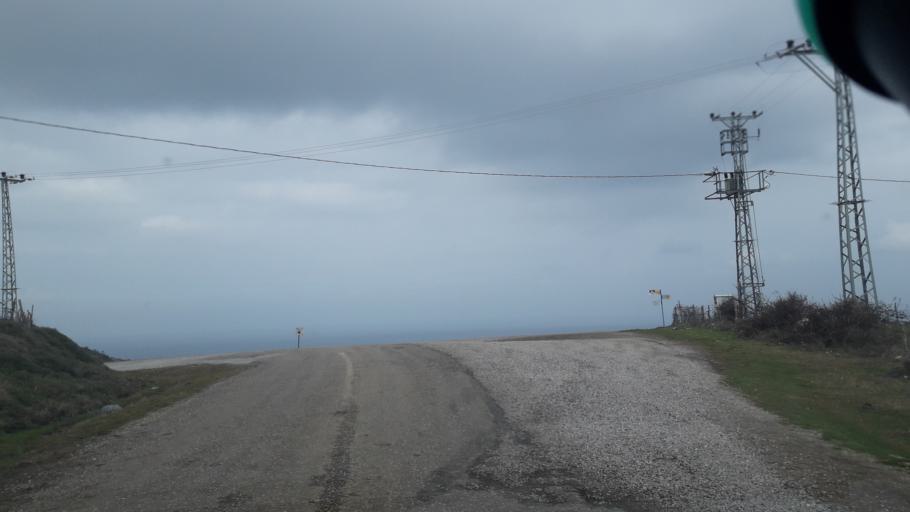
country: TR
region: Sinop
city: Sinop
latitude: 42.0195
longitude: 35.2044
